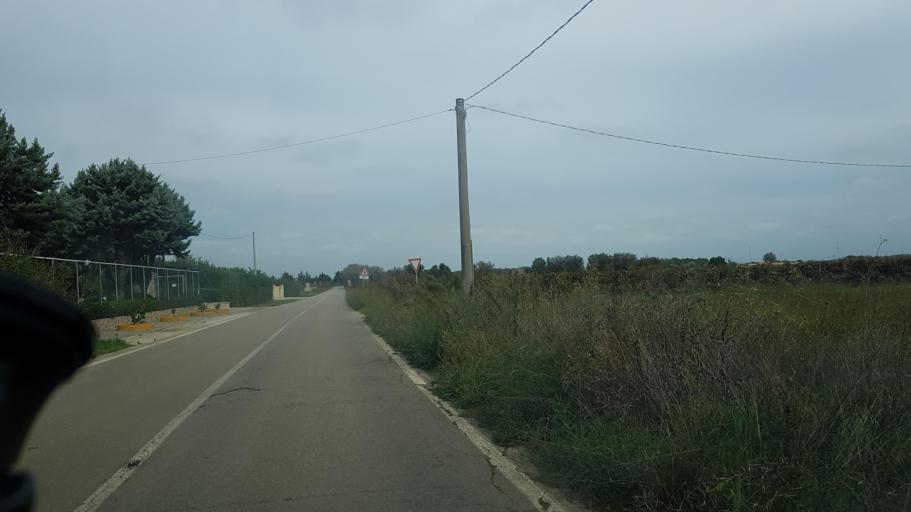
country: IT
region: Apulia
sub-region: Provincia di Lecce
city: Guagnano
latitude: 40.4098
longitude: 17.9495
